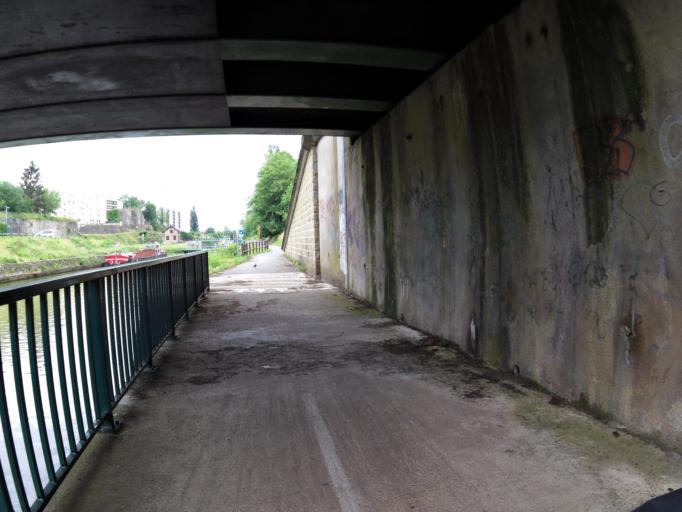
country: FR
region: Champagne-Ardenne
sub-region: Departement des Ardennes
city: Charleville-Mezieres
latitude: 49.7584
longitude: 4.7255
